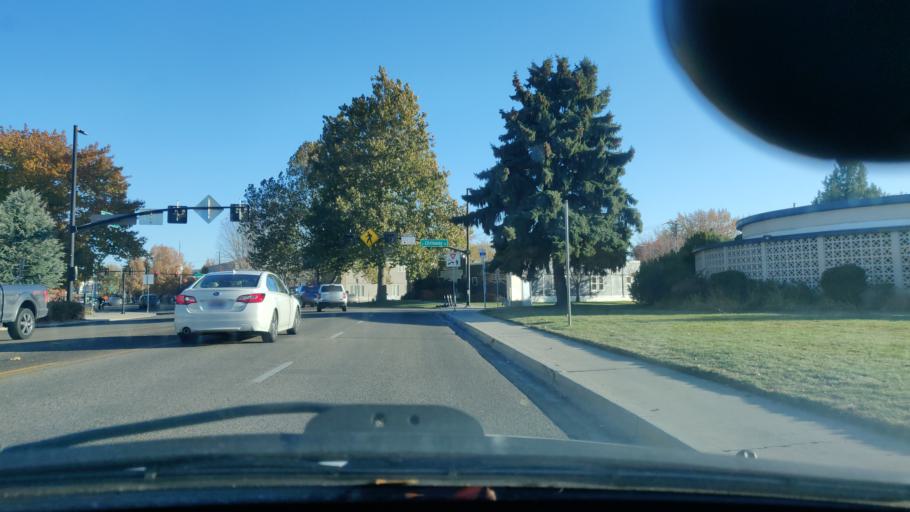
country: US
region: Idaho
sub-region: Ada County
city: Boise
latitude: 43.6042
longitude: -116.2074
